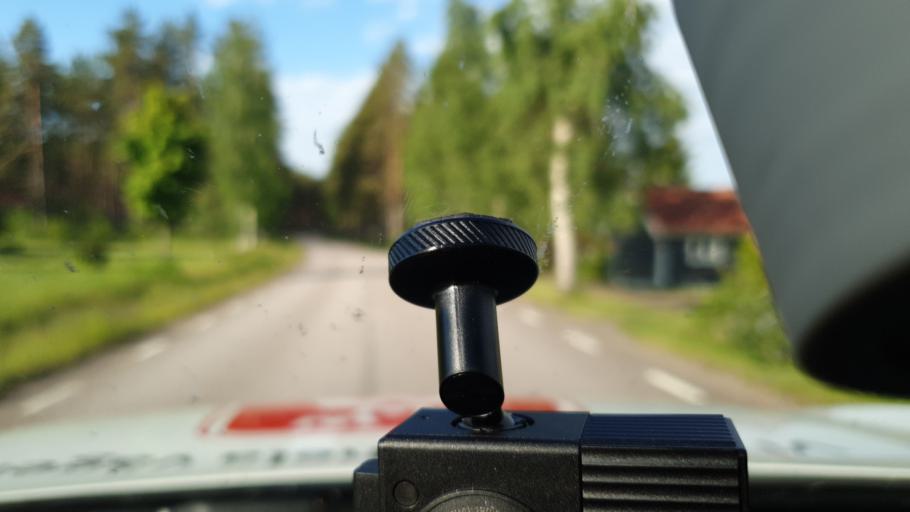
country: SE
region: Vaermland
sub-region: Torsby Kommun
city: Torsby
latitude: 60.0027
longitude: 12.8971
